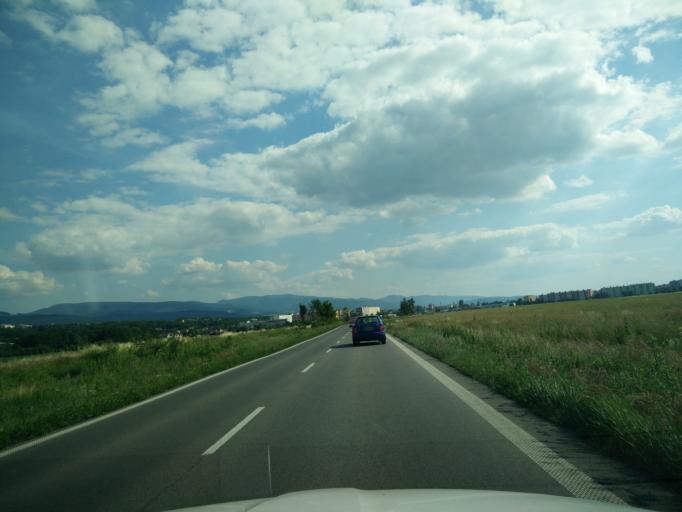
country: SK
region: Nitriansky
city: Prievidza
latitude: 48.7964
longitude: 18.6331
